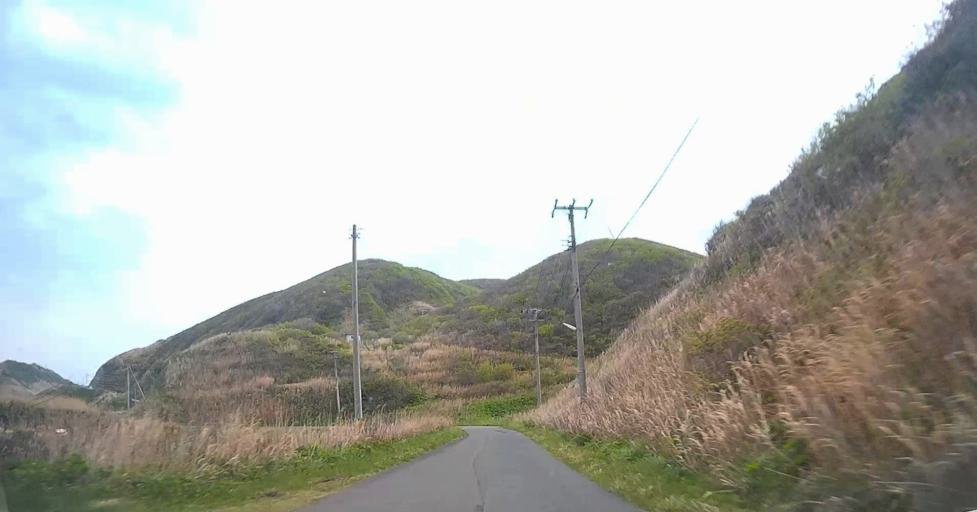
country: JP
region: Aomori
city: Shimokizukuri
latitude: 41.2453
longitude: 140.3432
